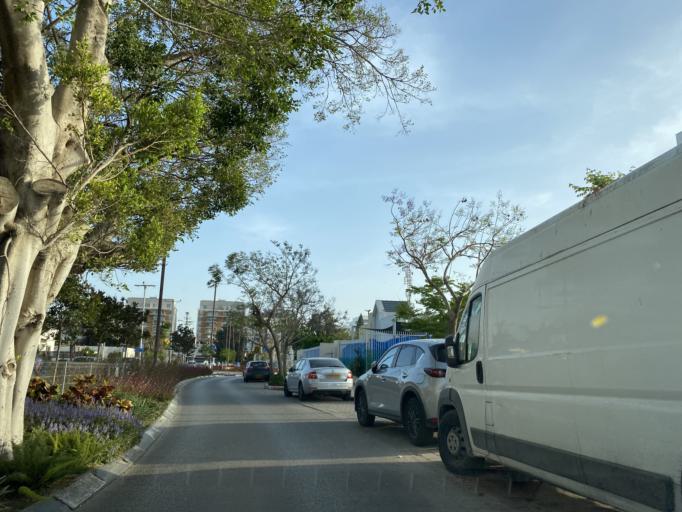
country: IL
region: Tel Aviv
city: Herzliyya
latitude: 32.1645
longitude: 34.8304
